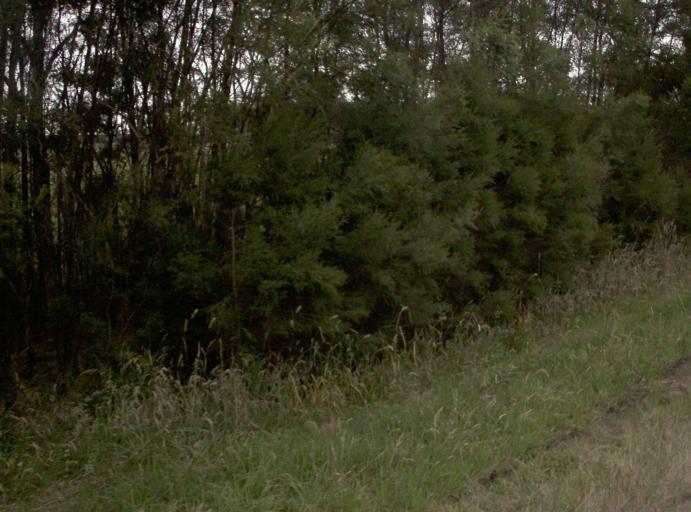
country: AU
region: Victoria
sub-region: Latrobe
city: Traralgon
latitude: -38.5567
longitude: 146.7791
